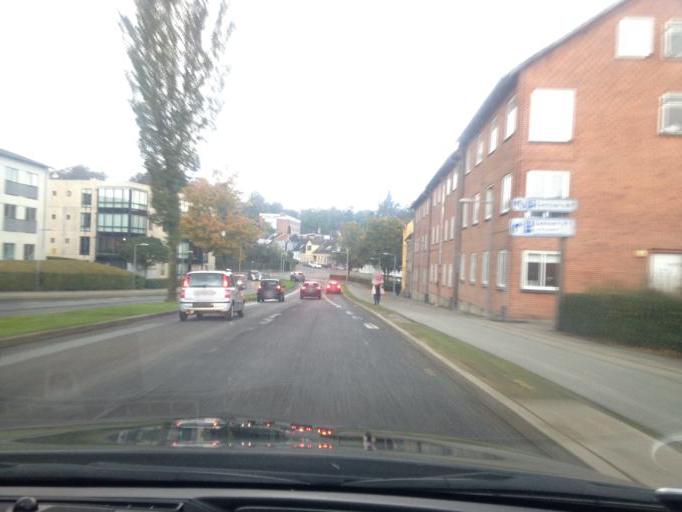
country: DK
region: South Denmark
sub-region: Kolding Kommune
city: Kolding
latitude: 55.4931
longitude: 9.4656
